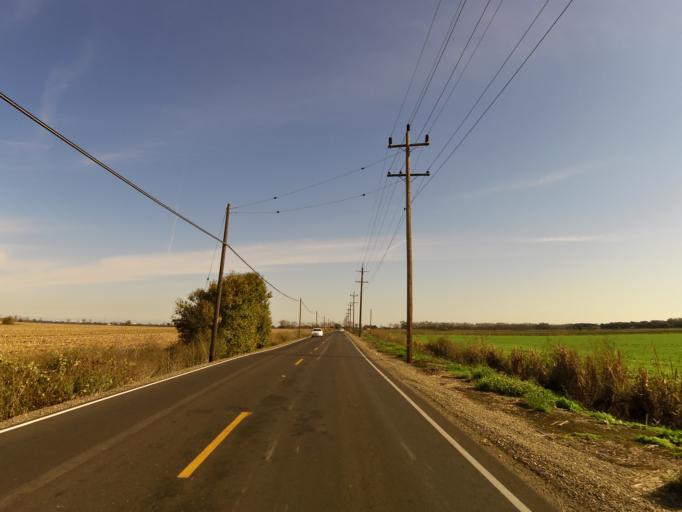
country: US
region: California
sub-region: Sacramento County
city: Walnut Grove
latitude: 38.2770
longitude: -121.4784
